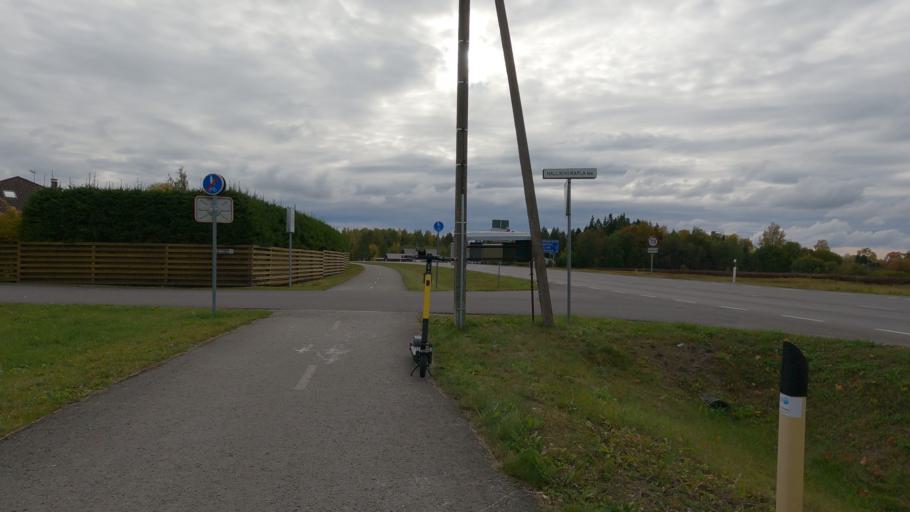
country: EE
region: Raplamaa
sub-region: Rapla vald
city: Rapla
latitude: 58.9932
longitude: 24.7863
